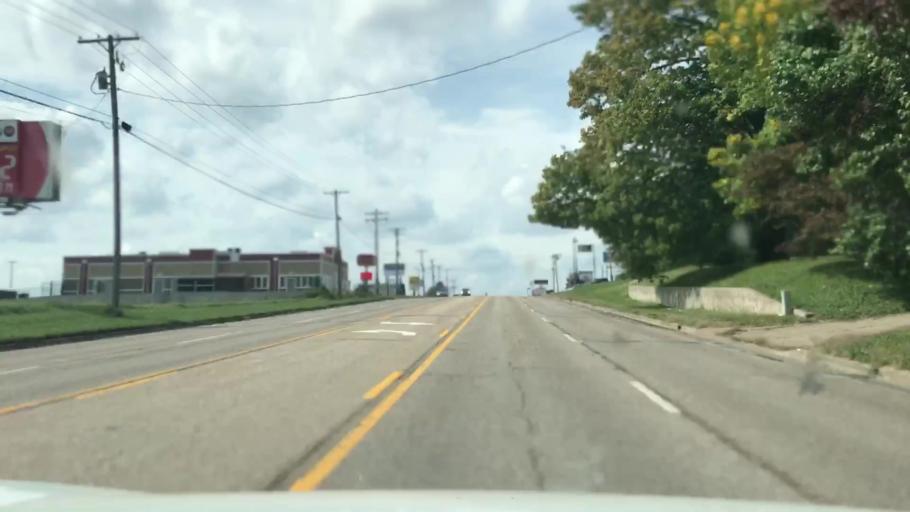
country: US
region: Illinois
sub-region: Adams County
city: Quincy
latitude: 39.9352
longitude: -91.3510
